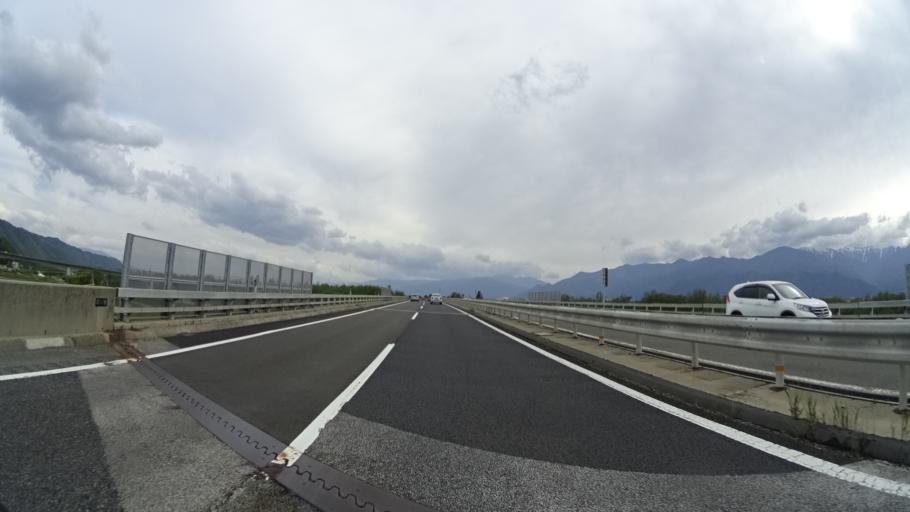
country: JP
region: Nagano
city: Toyoshina
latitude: 36.3223
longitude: 137.9225
